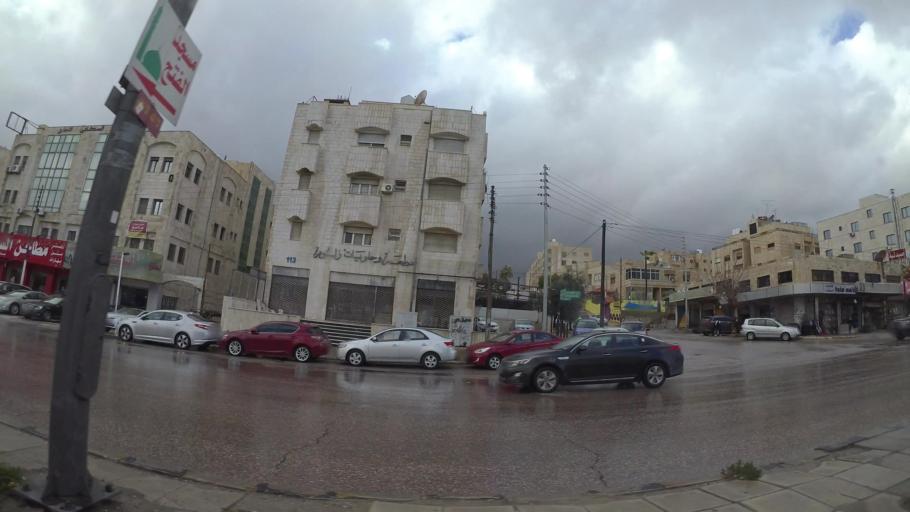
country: JO
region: Amman
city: Amman
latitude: 31.9905
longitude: 35.9114
